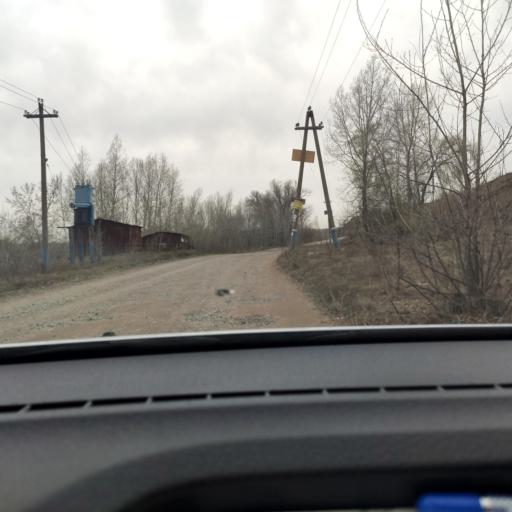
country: RU
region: Bashkortostan
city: Avdon
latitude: 54.6057
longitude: 55.6090
